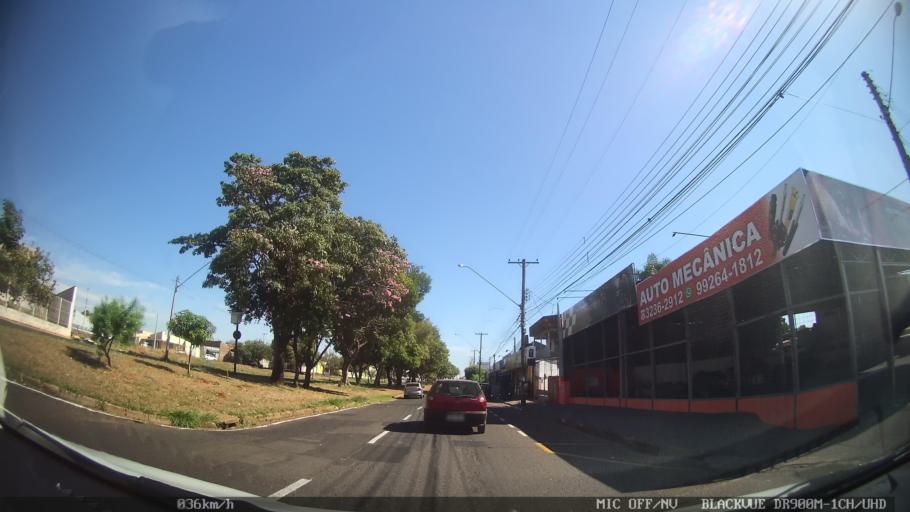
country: BR
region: Sao Paulo
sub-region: Sao Jose Do Rio Preto
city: Sao Jose do Rio Preto
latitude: -20.7751
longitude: -49.4119
